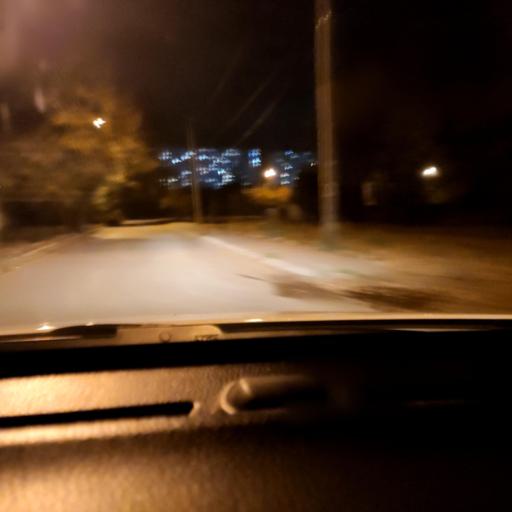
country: RU
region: Voronezj
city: Podgornoye
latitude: 51.7305
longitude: 39.1958
